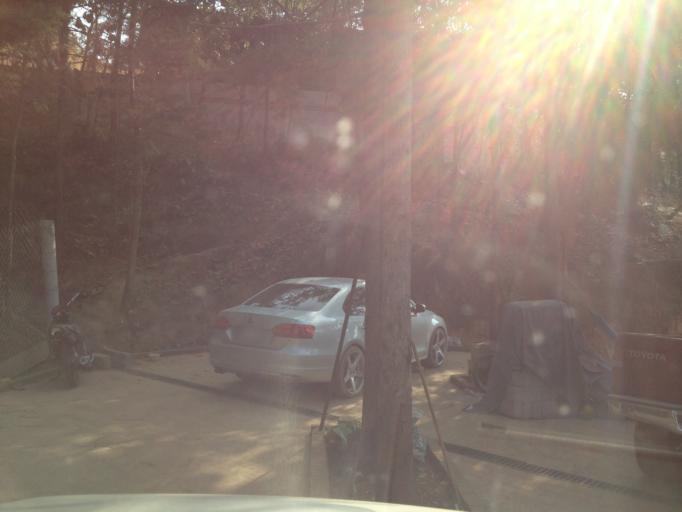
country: MX
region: Michoacan
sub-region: Zitacuaro
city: Macutzio
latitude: 19.4967
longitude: -100.3204
